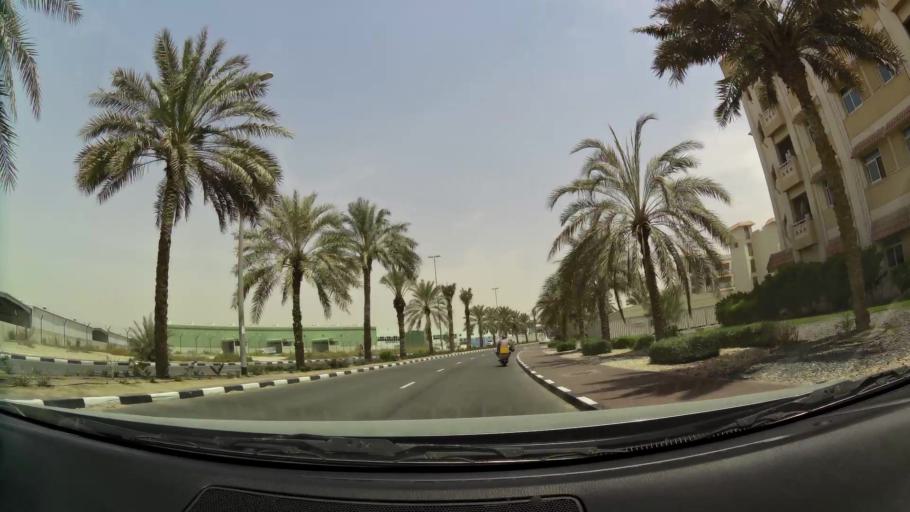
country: AE
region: Ash Shariqah
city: Sharjah
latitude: 25.1721
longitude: 55.4153
